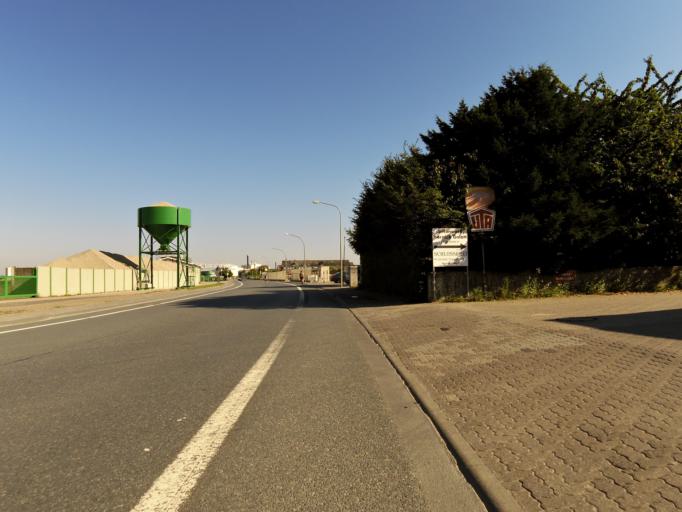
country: DE
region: Hesse
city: Gernsheim
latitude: 49.7598
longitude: 8.4832
